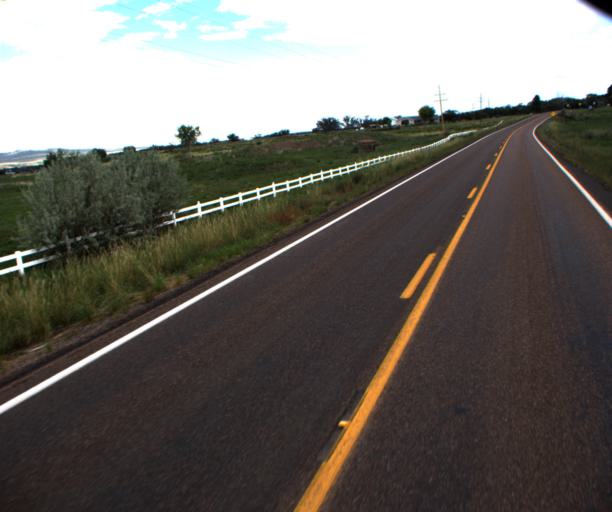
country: US
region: Arizona
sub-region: Apache County
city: Eagar
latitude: 34.1109
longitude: -109.3098
